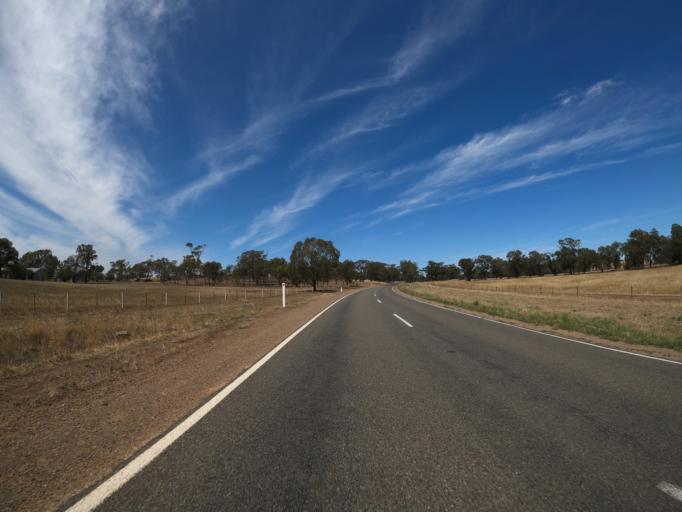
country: AU
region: Victoria
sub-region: Benalla
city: Benalla
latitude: -36.3306
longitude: 145.9614
